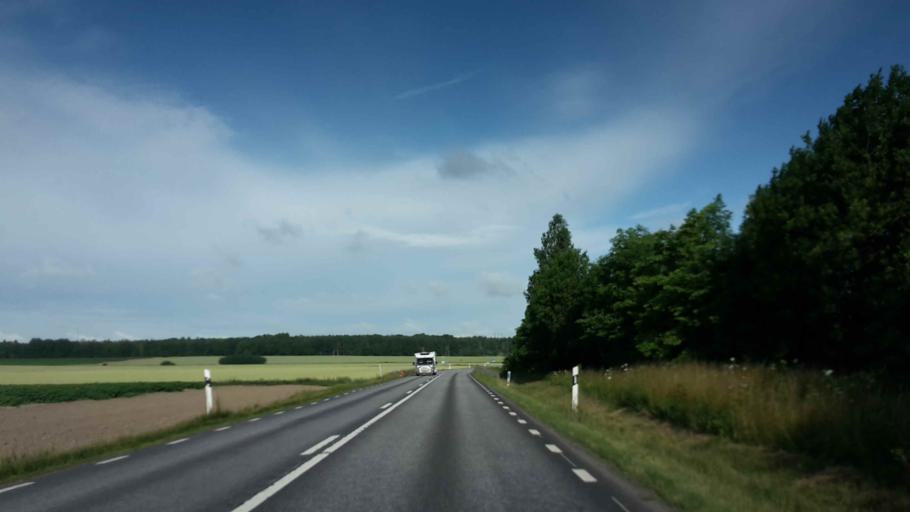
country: SE
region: OEstergoetland
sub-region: Motala Kommun
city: Borensberg
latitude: 58.5350
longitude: 15.3352
